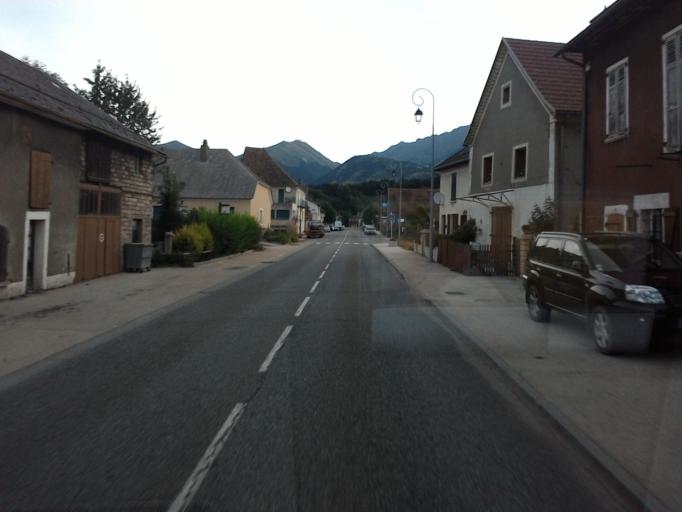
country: FR
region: Provence-Alpes-Cote d'Azur
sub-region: Departement des Hautes-Alpes
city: Saint-Bonnet-en-Champsaur
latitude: 44.7516
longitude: 6.0086
